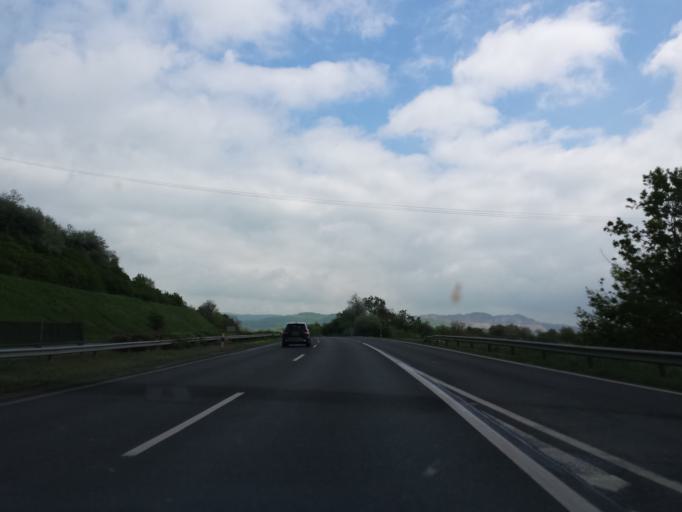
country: HU
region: Komarom-Esztergom
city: Tatabanya
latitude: 47.5779
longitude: 18.4158
